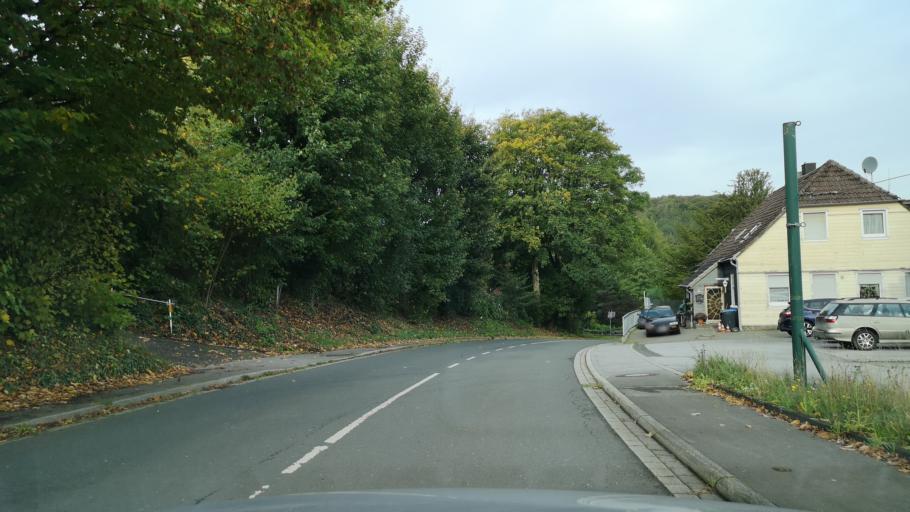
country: DE
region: North Rhine-Westphalia
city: Hattingen
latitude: 51.3378
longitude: 7.1761
